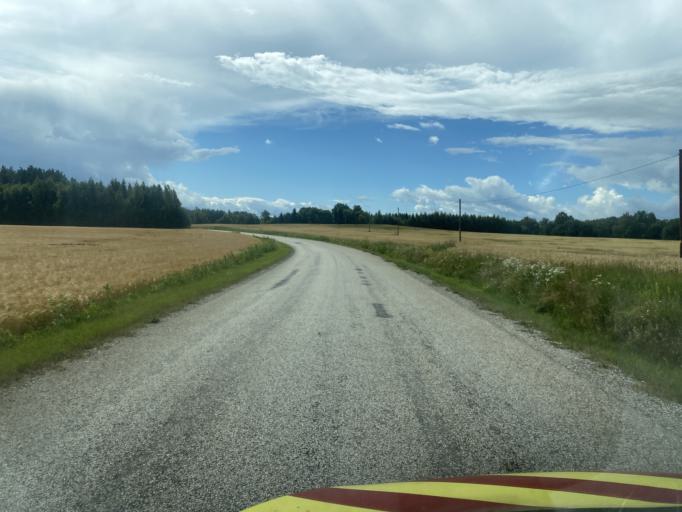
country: EE
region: Valgamaa
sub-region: Torva linn
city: Torva
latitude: 57.9552
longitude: 25.8847
